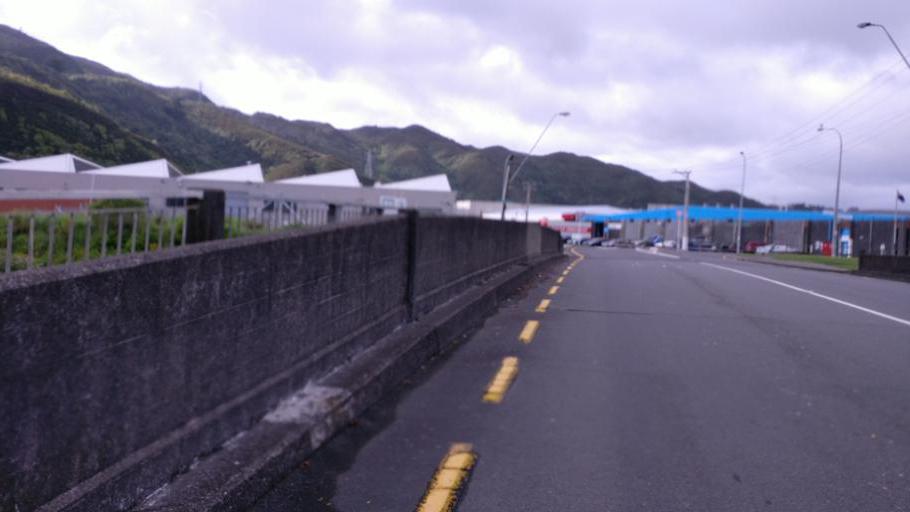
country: NZ
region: Wellington
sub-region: Lower Hutt City
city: Lower Hutt
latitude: -41.2335
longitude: 174.9145
